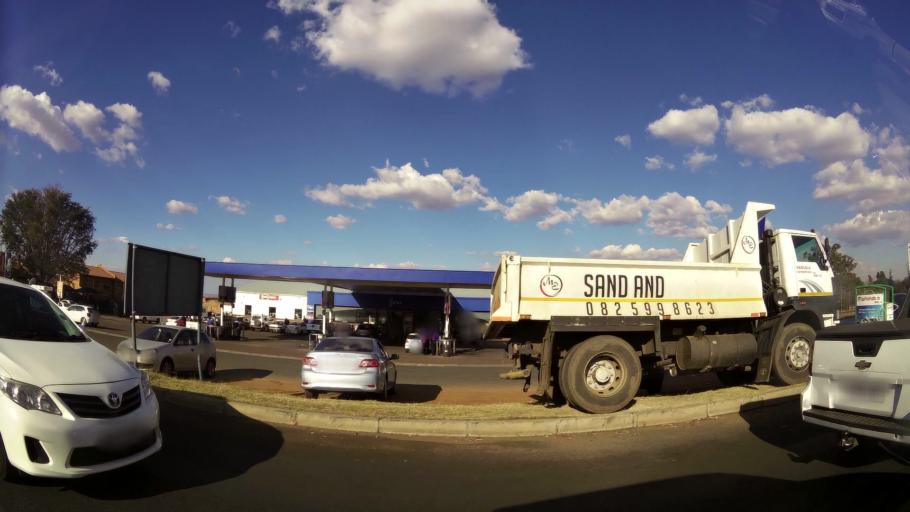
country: ZA
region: Mpumalanga
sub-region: Nkangala District Municipality
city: Witbank
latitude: -25.8869
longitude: 29.2330
